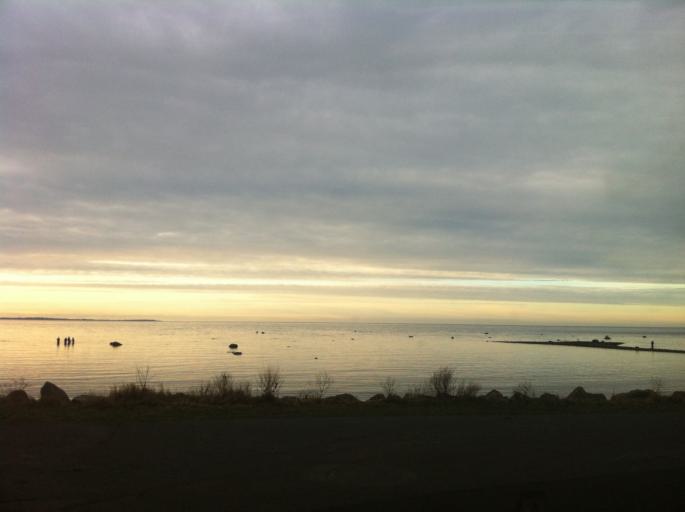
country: SE
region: Skane
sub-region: Hoganas Kommun
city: Hoganas
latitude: 56.1914
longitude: 12.5547
